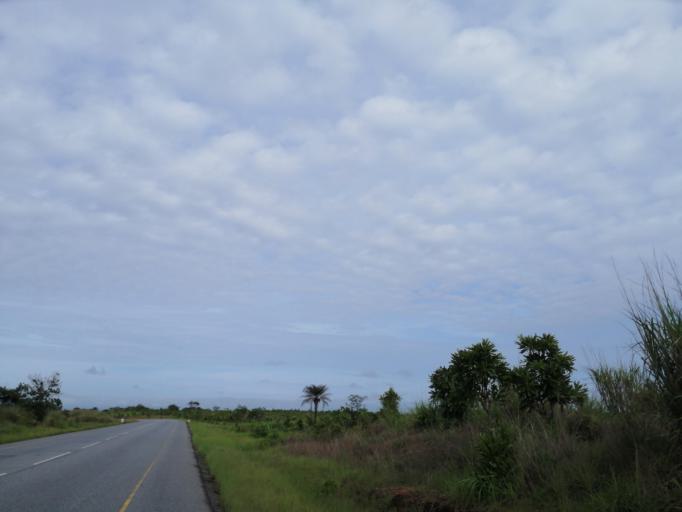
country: SL
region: Northern Province
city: Port Loko
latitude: 8.7829
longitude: -12.8538
